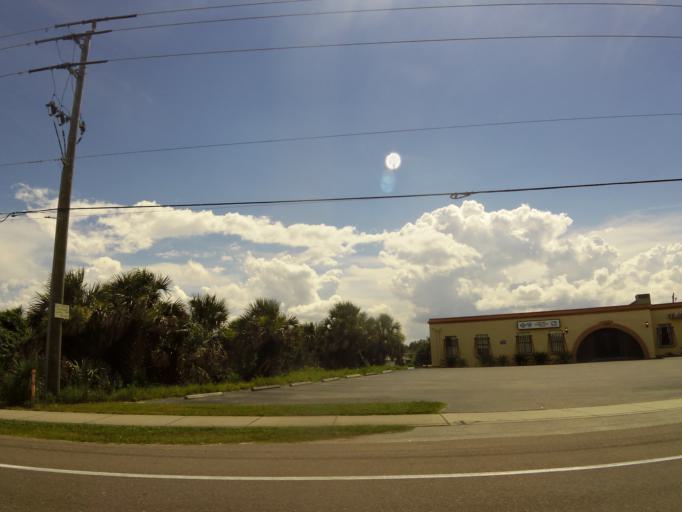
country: US
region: Florida
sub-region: Volusia County
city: Ormond-by-the-Sea
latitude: 29.3211
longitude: -81.0543
